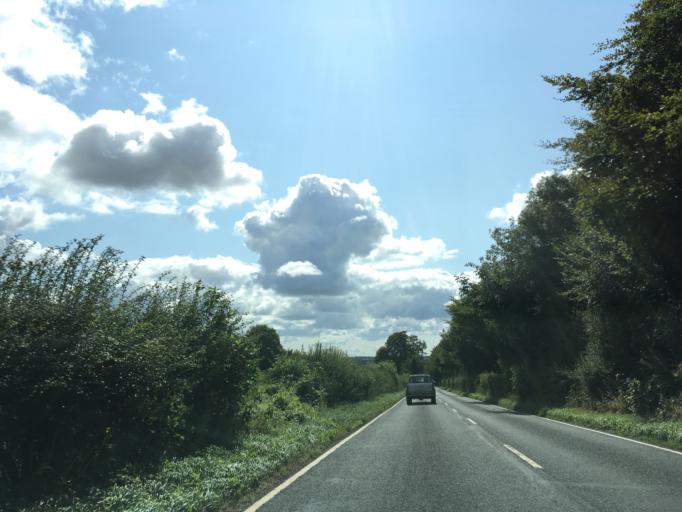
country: GB
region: England
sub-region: Hampshire
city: Winchester
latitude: 51.0383
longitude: -1.2826
